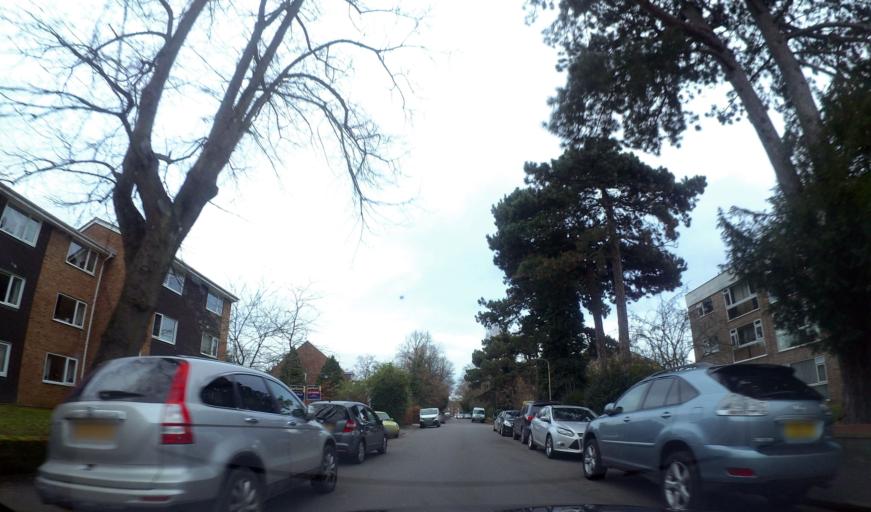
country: GB
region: England
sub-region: Reading
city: Reading
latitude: 51.4493
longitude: -0.9954
